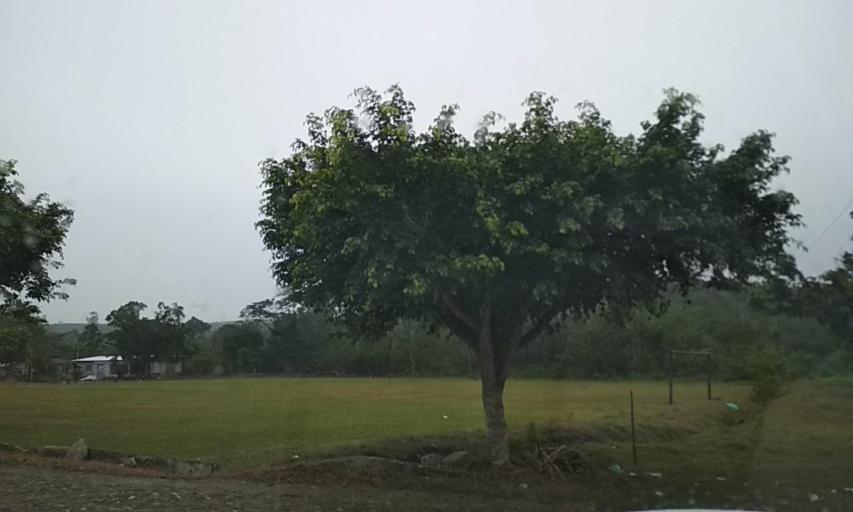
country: MX
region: Veracruz
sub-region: Papantla
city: El Chote
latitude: 20.3318
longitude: -97.3942
